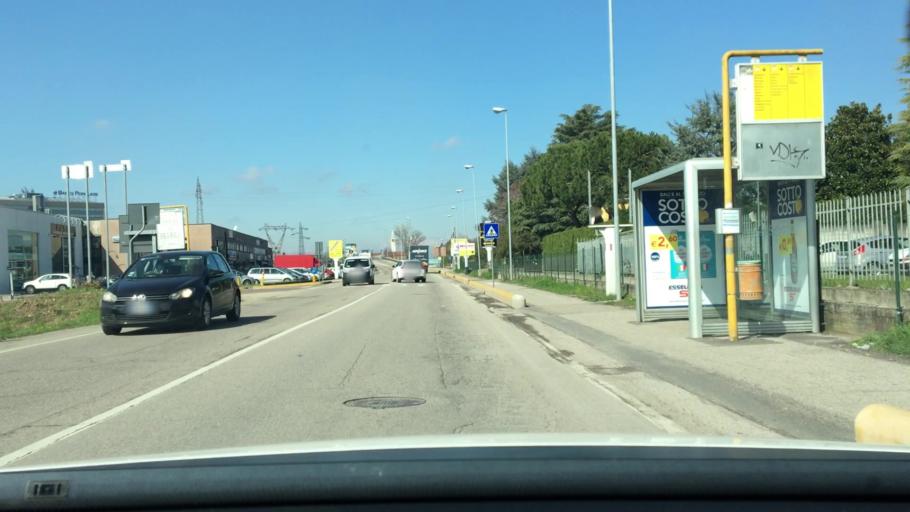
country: IT
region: Veneto
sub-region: Provincia di Verona
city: San Giovanni Lupatoto
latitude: 45.3981
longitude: 11.0233
